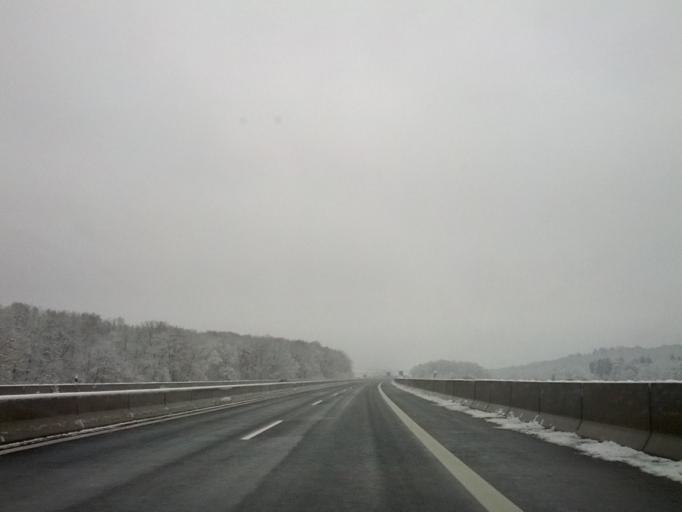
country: DE
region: Bavaria
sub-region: Regierungsbezirk Unterfranken
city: Rannungen
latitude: 50.1878
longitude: 10.2014
